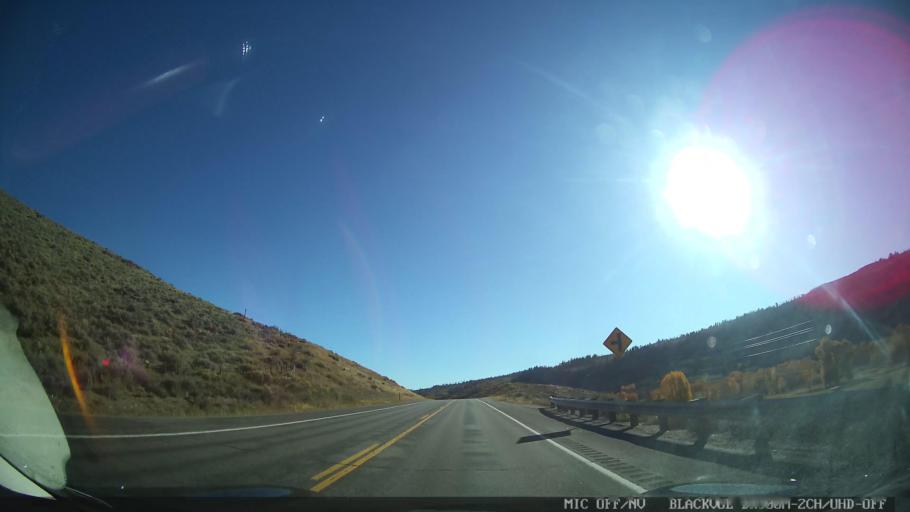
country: US
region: Colorado
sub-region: Grand County
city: Hot Sulphur Springs
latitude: 40.0991
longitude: -106.0360
